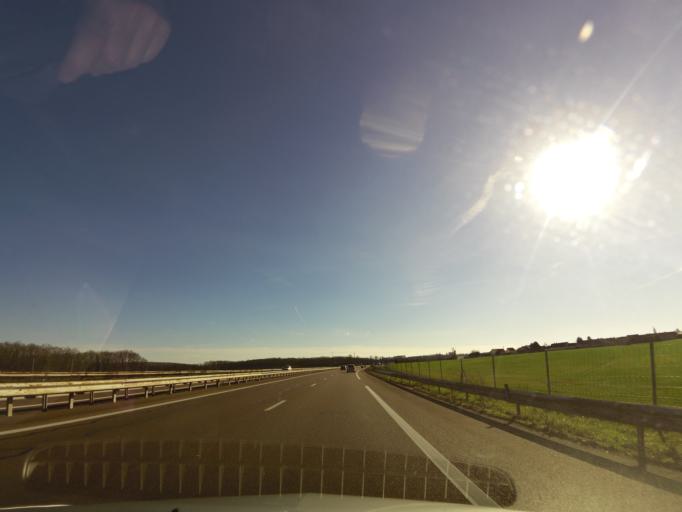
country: FR
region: Bourgogne
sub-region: Departement de l'Yonne
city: Venoy
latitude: 47.8328
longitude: 3.6214
